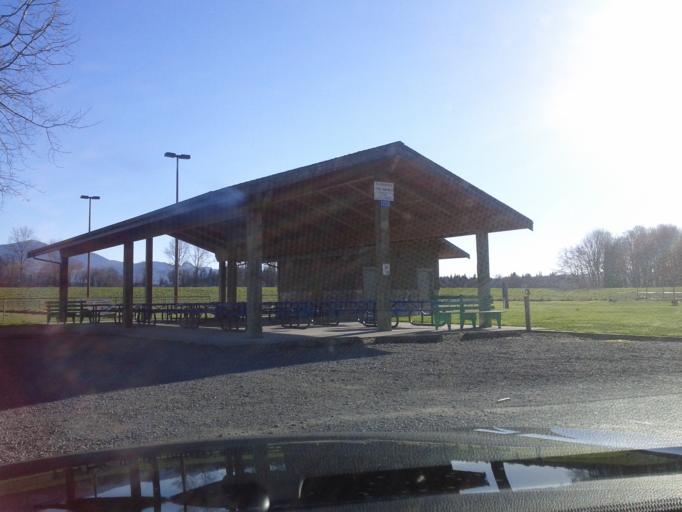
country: US
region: Washington
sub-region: Skagit County
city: Burlington
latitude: 48.4536
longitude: -122.3244
